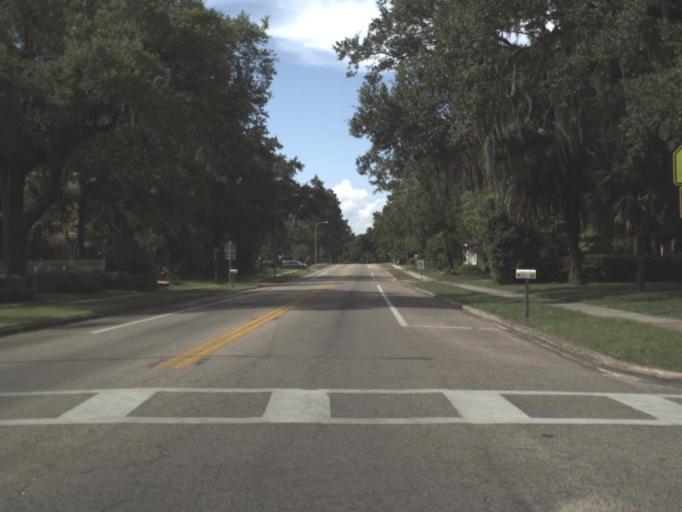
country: US
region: Florida
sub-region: Taylor County
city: Perry
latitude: 30.1220
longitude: -83.5820
